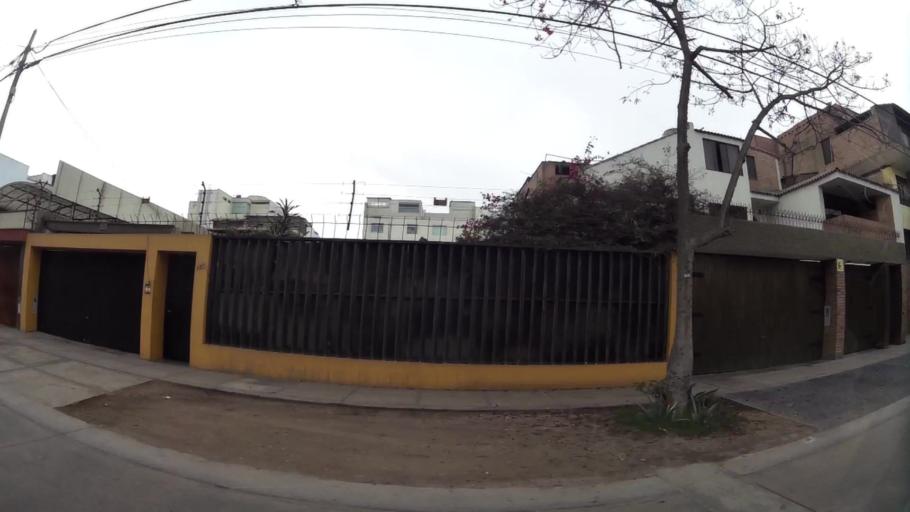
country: PE
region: Lima
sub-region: Lima
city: San Luis
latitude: -12.1042
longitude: -76.9805
